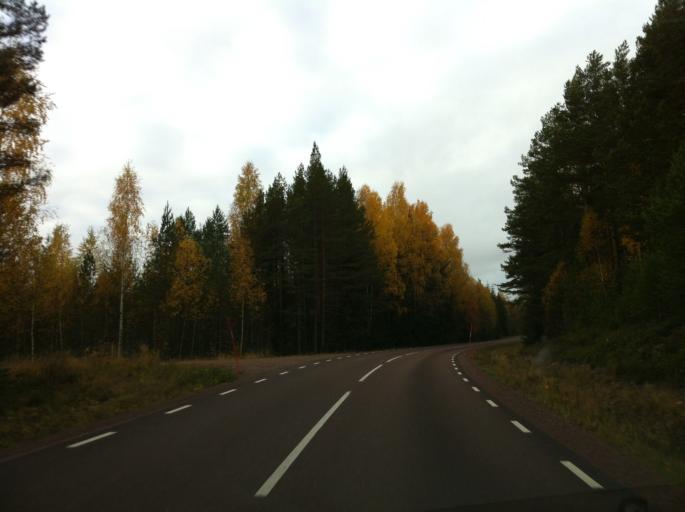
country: SE
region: Dalarna
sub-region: Orsa Kommun
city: Orsa
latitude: 61.1261
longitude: 14.5222
